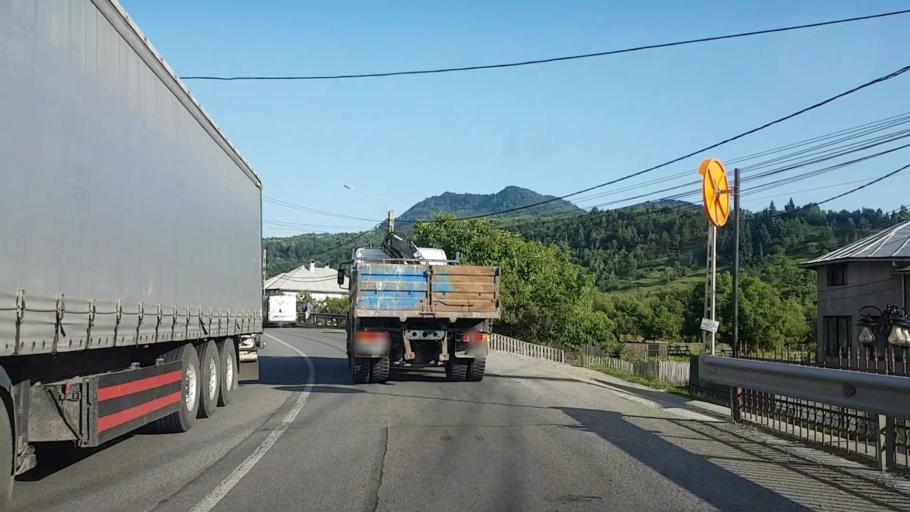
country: RO
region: Bistrita-Nasaud
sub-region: Comuna Tiha Bargaului
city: Tureac
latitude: 47.2283
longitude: 24.8058
